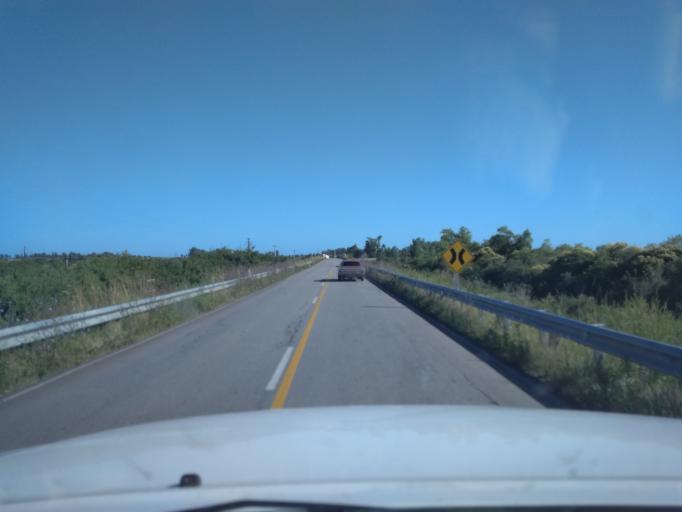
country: UY
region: Canelones
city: San Ramon
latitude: -34.3254
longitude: -55.9613
